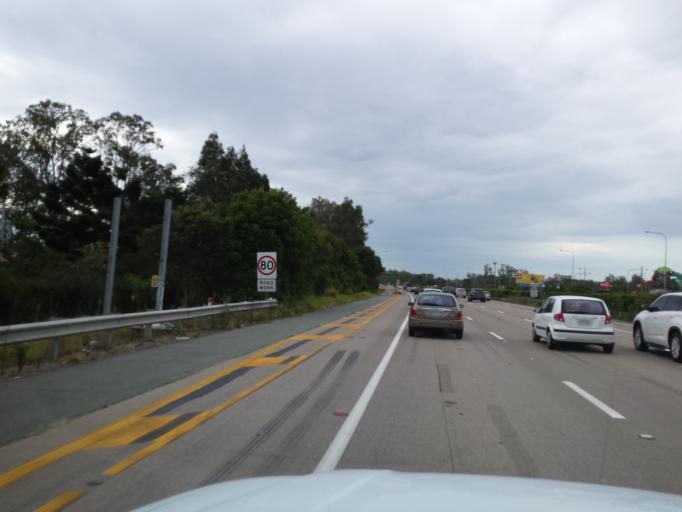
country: AU
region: Queensland
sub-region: Gold Coast
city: Oxenford
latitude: -27.8685
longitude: 153.3129
